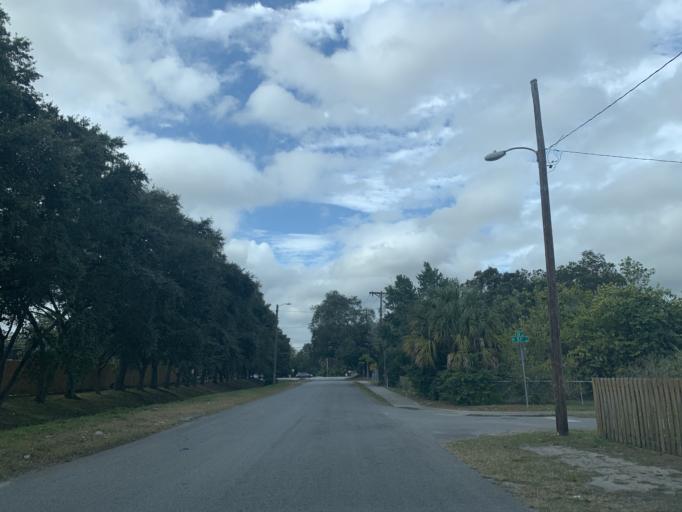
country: US
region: Florida
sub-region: Hillsborough County
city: East Lake-Orient Park
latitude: 27.9743
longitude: -82.4000
